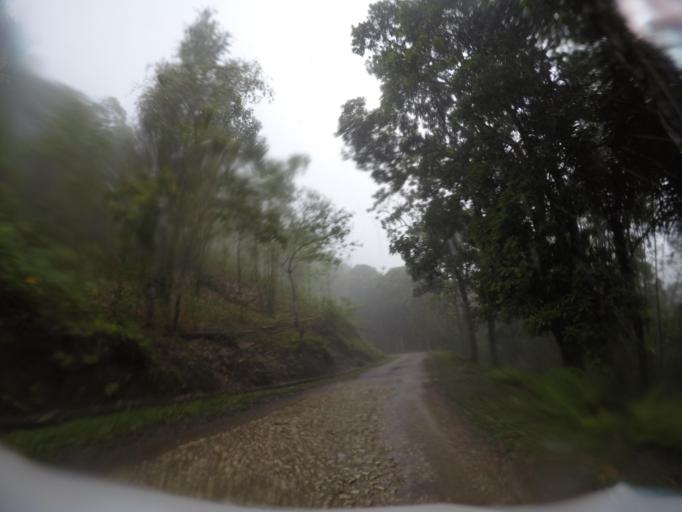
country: TL
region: Baucau
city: Venilale
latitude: -8.6419
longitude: 126.4037
